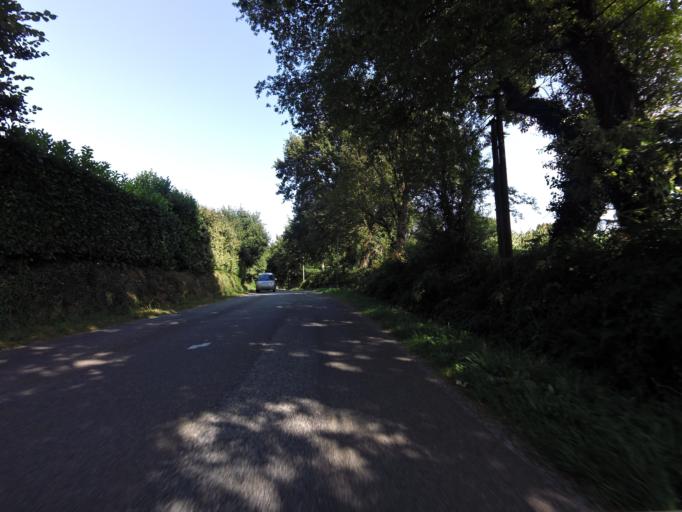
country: FR
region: Brittany
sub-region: Departement du Morbihan
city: Questembert
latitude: 47.6596
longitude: -2.4230
